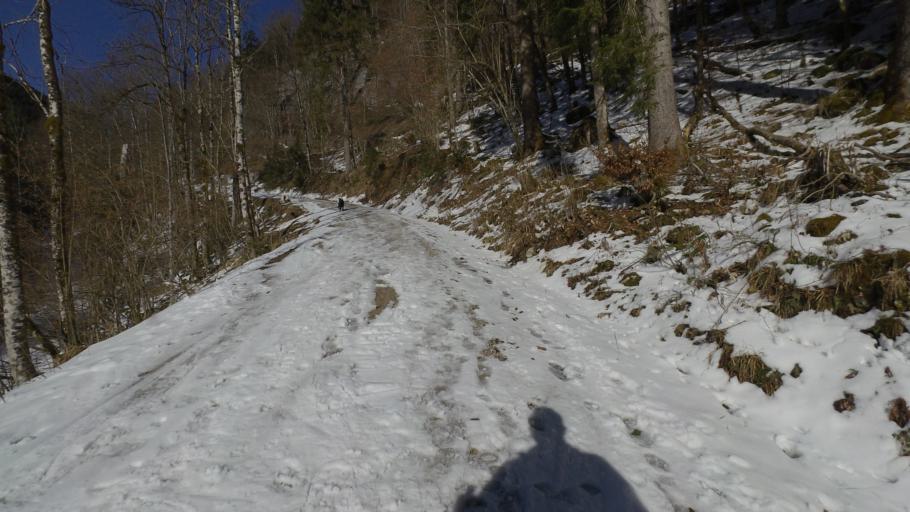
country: DE
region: Bavaria
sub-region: Upper Bavaria
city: Ruhpolding
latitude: 47.7509
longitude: 12.6004
